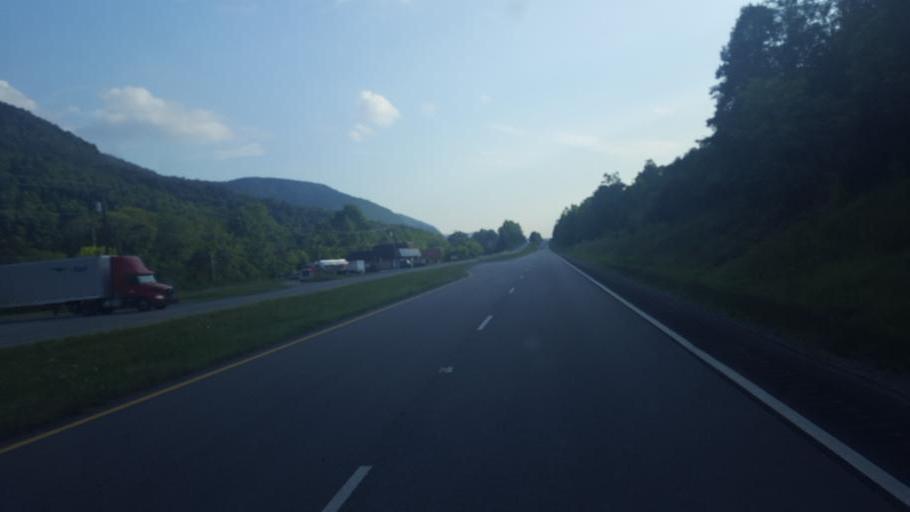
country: US
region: Virginia
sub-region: Wise County
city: Big Stone Gap
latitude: 36.8198
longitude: -82.7781
